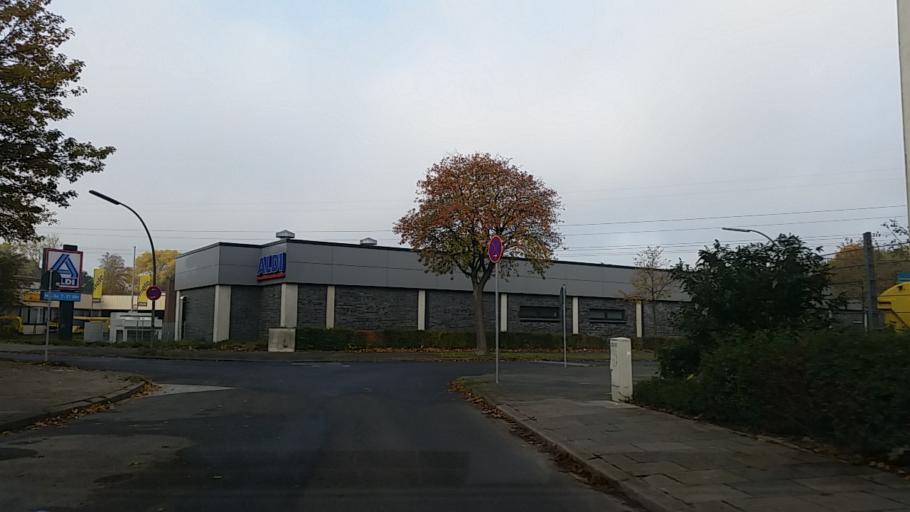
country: DE
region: Hamburg
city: Wandsbek
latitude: 53.5572
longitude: 10.1039
